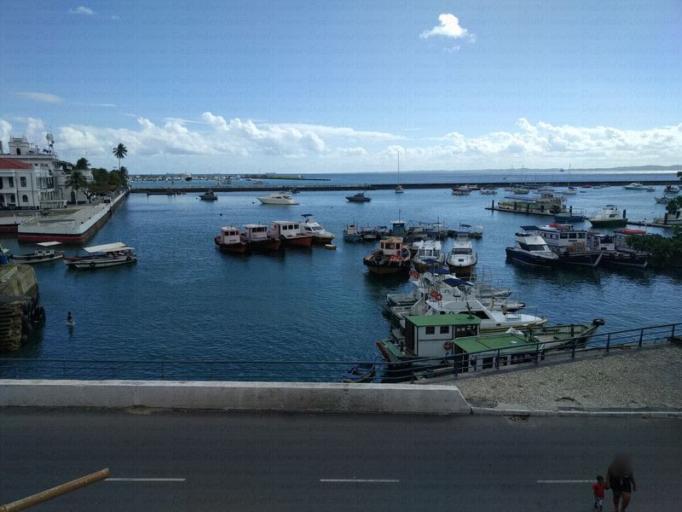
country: BR
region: Bahia
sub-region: Salvador
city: Salvador
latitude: -12.9728
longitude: -38.5142
